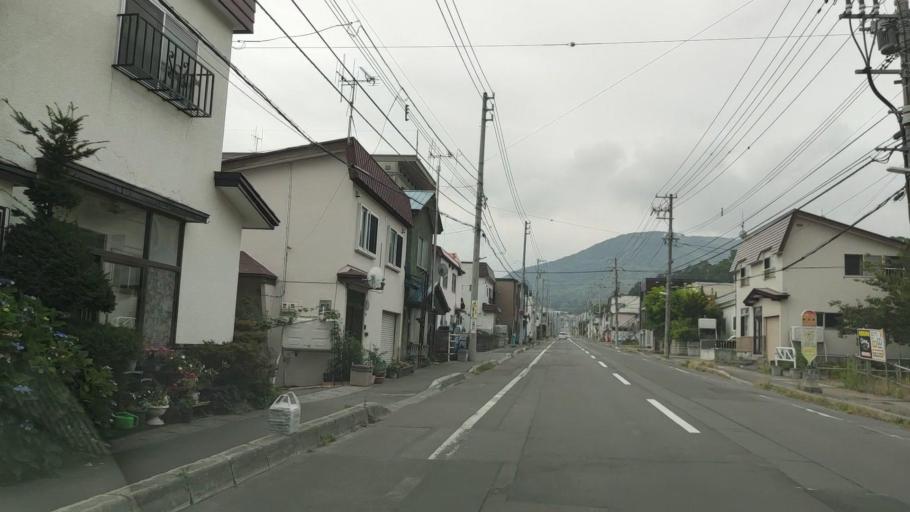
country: JP
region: Hokkaido
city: Otaru
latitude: 43.1914
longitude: 140.9880
